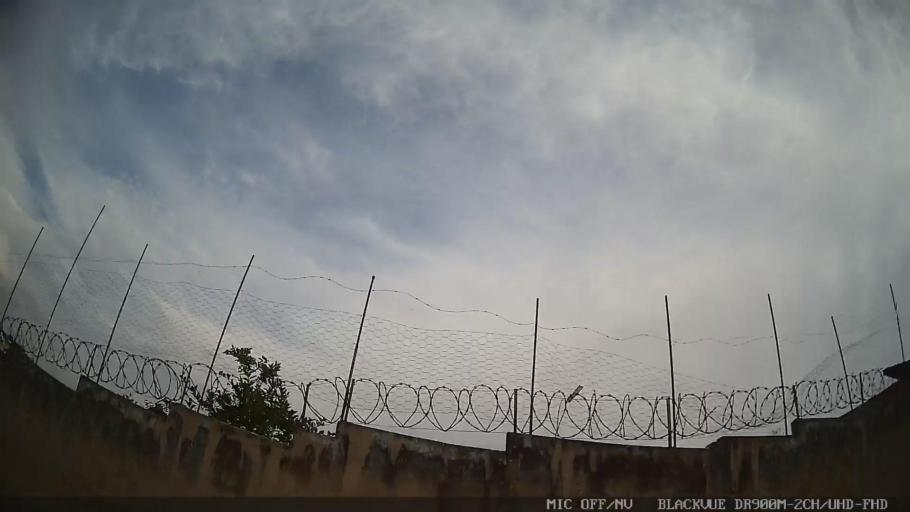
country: BR
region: Sao Paulo
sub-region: Braganca Paulista
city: Braganca Paulista
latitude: -22.9488
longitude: -46.5466
